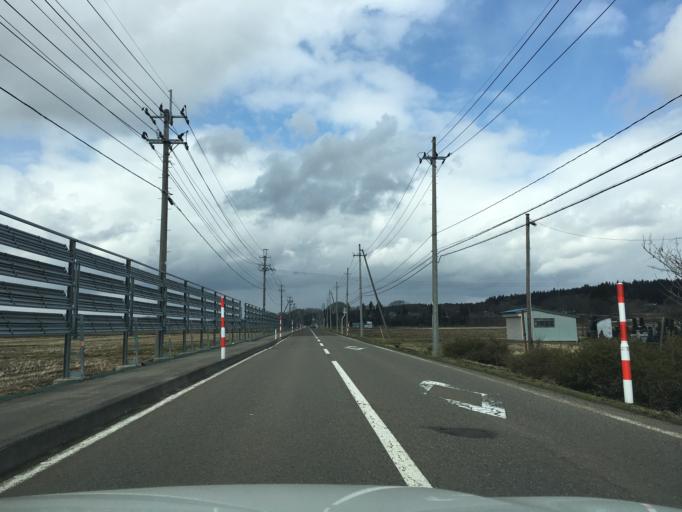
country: JP
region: Akita
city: Takanosu
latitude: 40.1376
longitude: 140.3528
